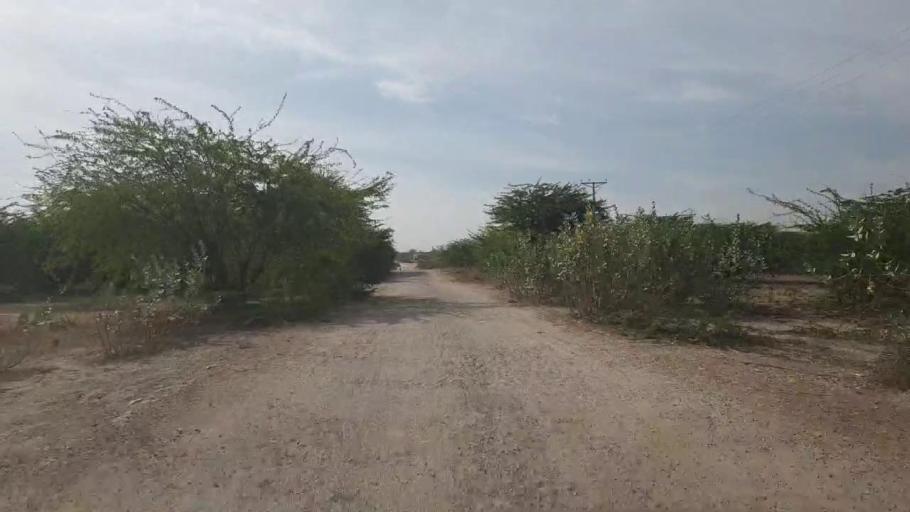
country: PK
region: Sindh
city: Umarkot
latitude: 25.2934
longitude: 69.7380
